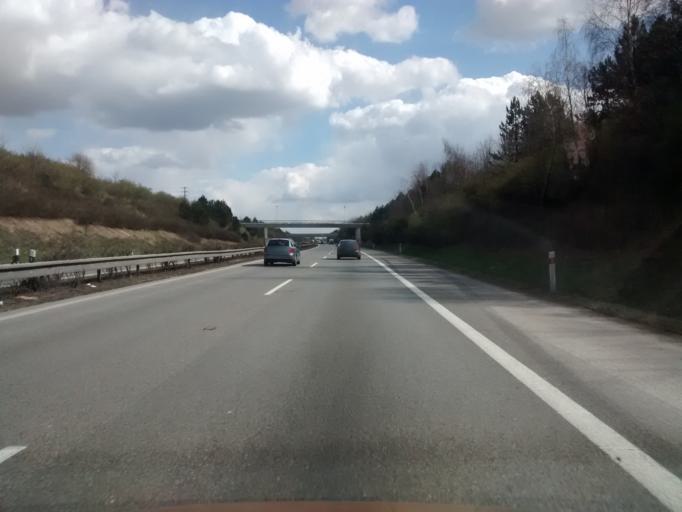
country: CZ
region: Central Bohemia
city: Odolena Voda
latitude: 50.2253
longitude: 14.4067
